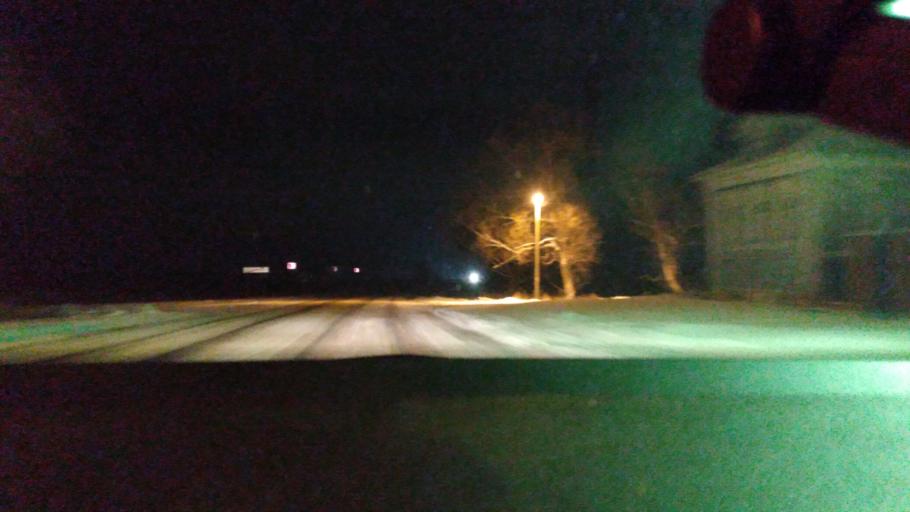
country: RU
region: Moskovskaya
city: Krasnaya Poyma
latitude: 55.0588
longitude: 39.1136
